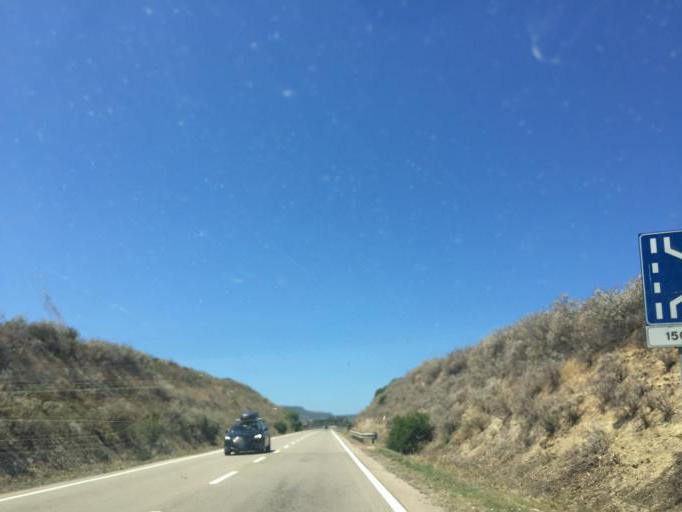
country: IT
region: Sardinia
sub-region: Provincia di Sassari
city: Codaruina
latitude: 40.9158
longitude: 8.8306
